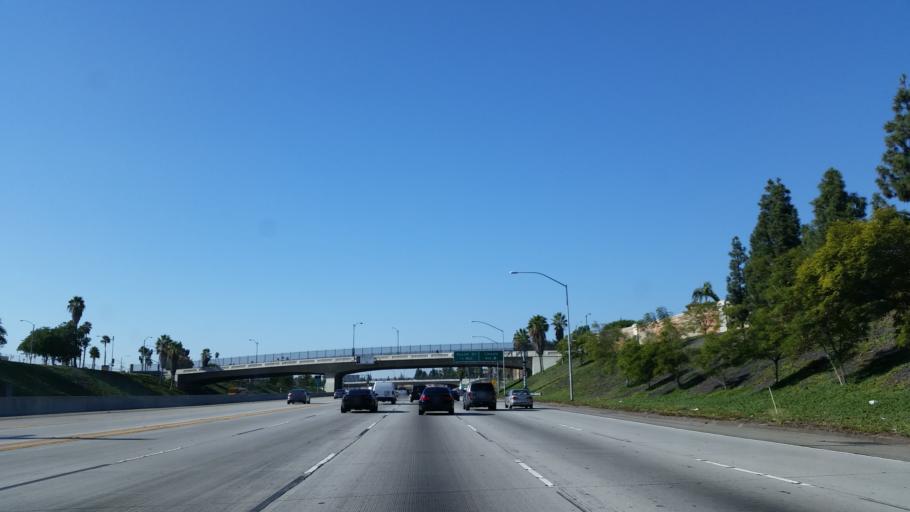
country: US
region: California
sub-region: Orange County
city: Anaheim
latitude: 33.8283
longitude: -117.9275
